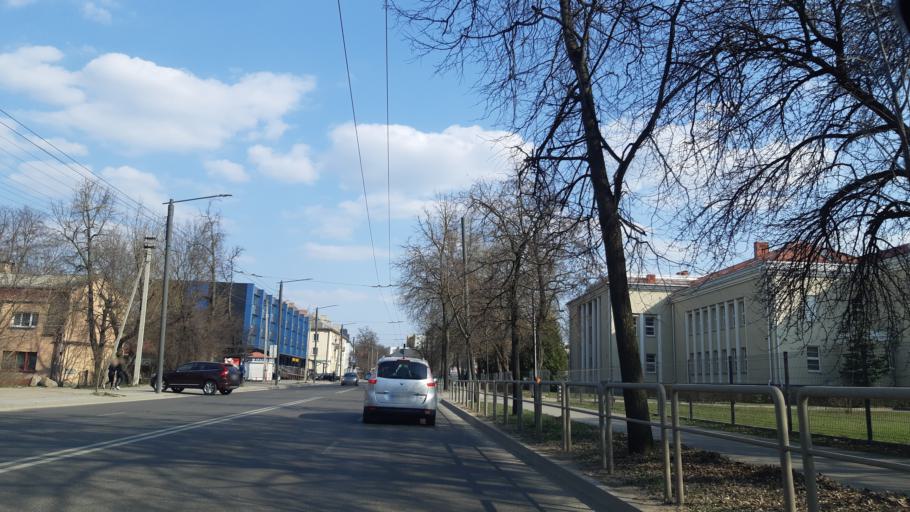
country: LT
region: Kauno apskritis
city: Dainava (Kaunas)
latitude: 54.8929
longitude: 23.9983
